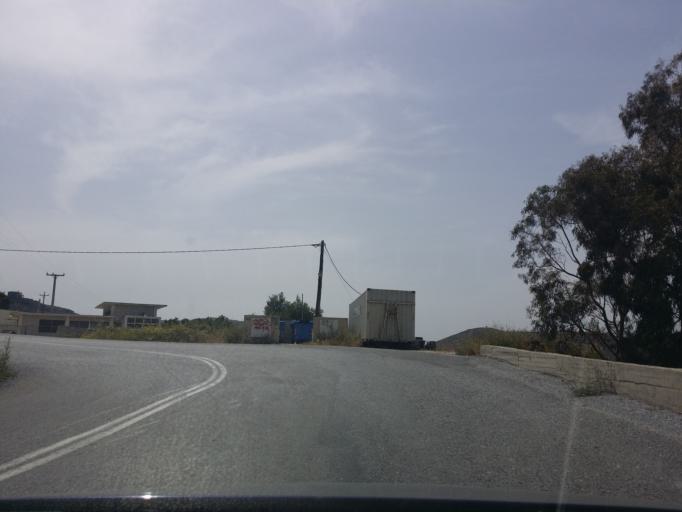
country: GR
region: South Aegean
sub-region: Nomos Kykladon
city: Kea
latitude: 37.6455
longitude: 24.3301
